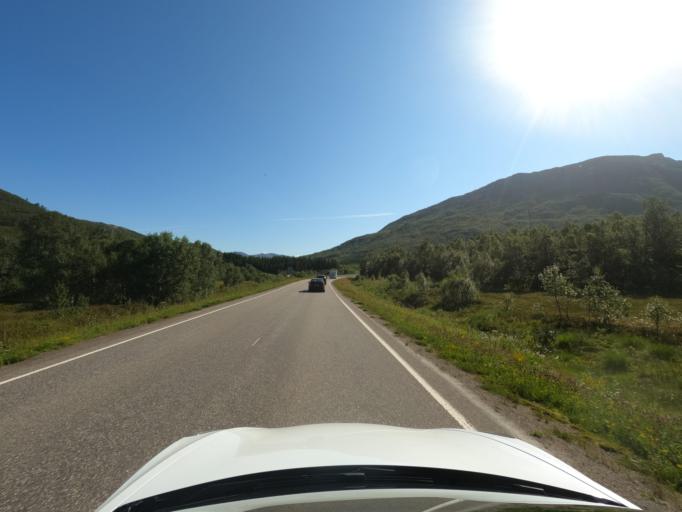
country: NO
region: Nordland
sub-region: Lodingen
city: Lodingen
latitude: 68.5296
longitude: 15.7464
